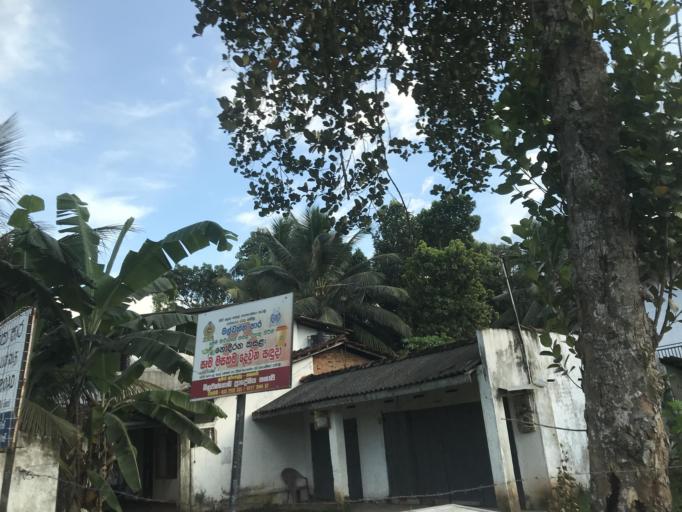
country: LK
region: Western
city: Gampaha
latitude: 7.1029
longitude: 79.9768
